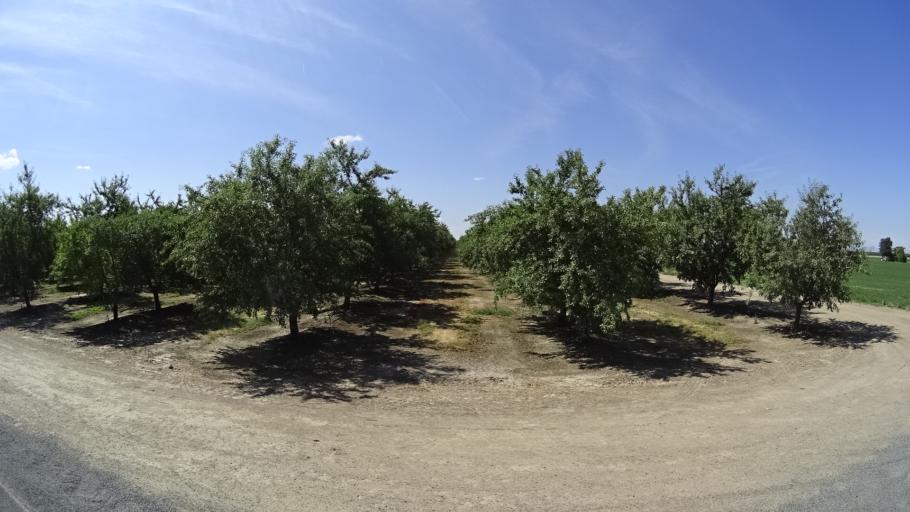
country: US
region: California
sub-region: Kings County
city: Armona
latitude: 36.2693
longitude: -119.7357
